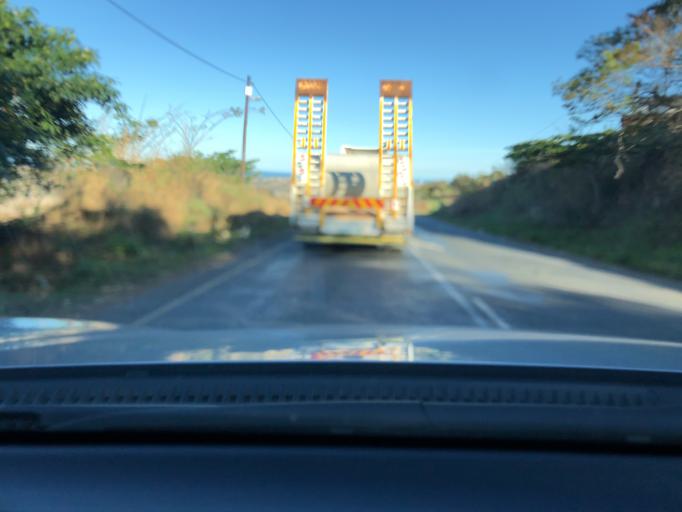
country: ZA
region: KwaZulu-Natal
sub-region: eThekwini Metropolitan Municipality
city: Umkomaas
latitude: -30.0212
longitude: 30.8103
